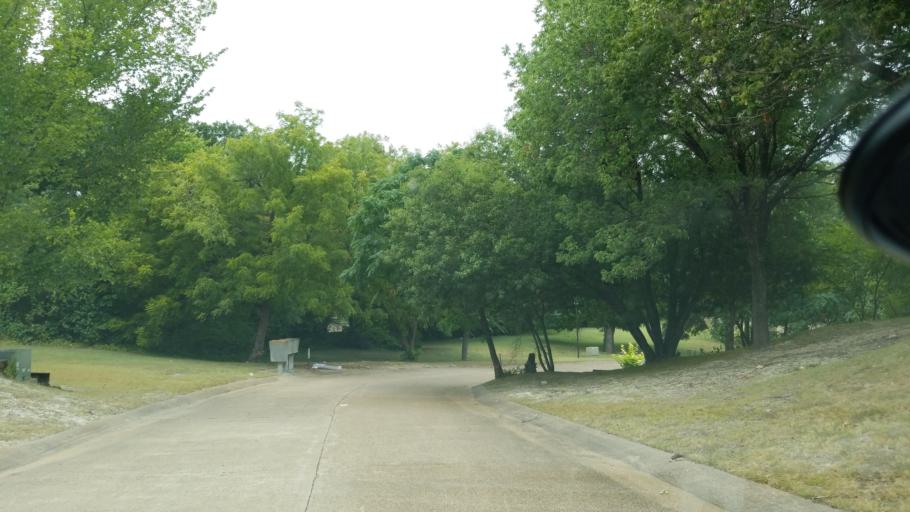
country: US
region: Texas
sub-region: Dallas County
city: Duncanville
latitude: 32.6627
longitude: -96.8497
